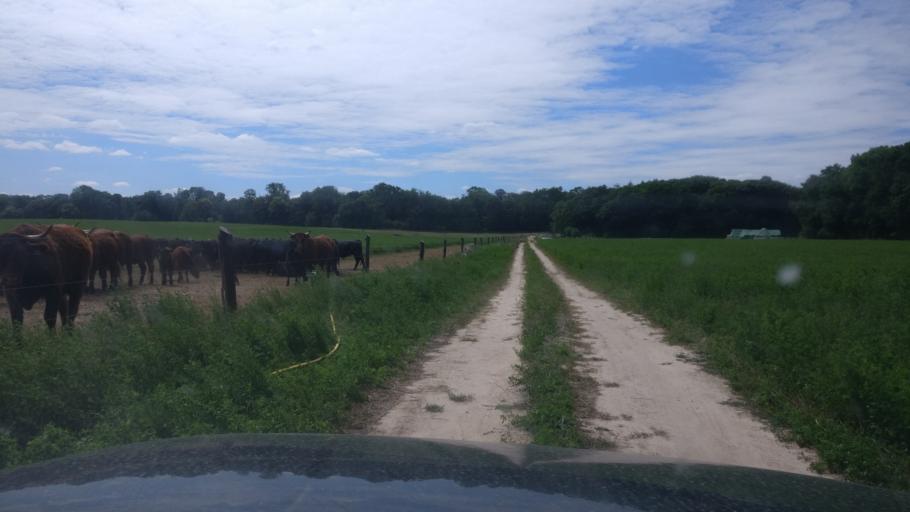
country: DE
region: Brandenburg
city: Briesen
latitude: 52.3924
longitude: 14.2848
